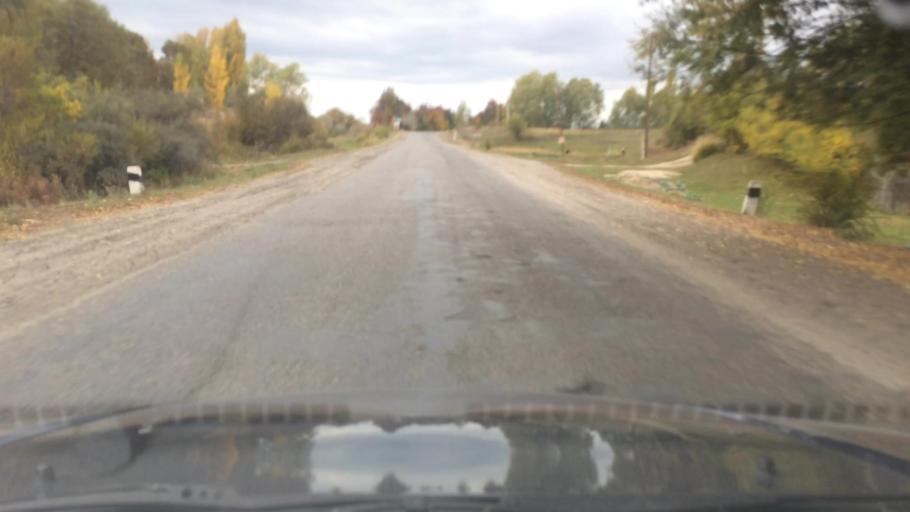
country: KG
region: Ysyk-Koel
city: Tyup
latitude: 42.7671
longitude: 78.1832
